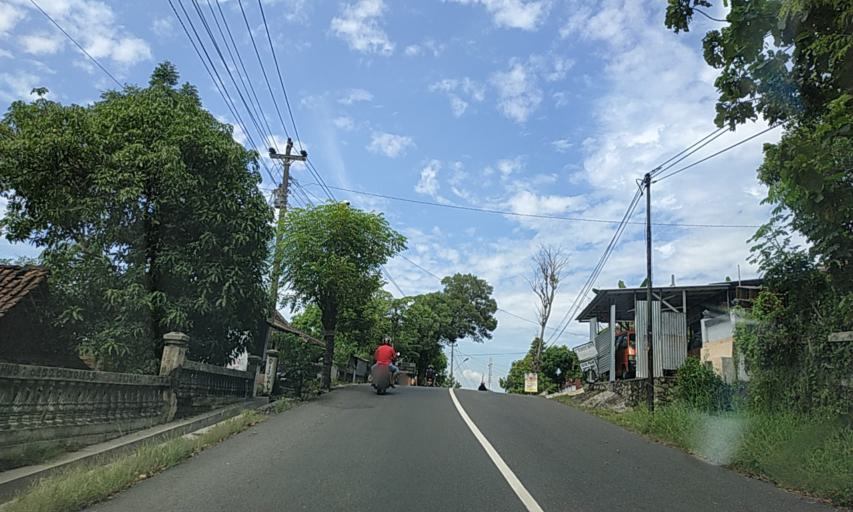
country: ID
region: Central Java
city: Selogiri
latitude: -7.8081
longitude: 110.9265
